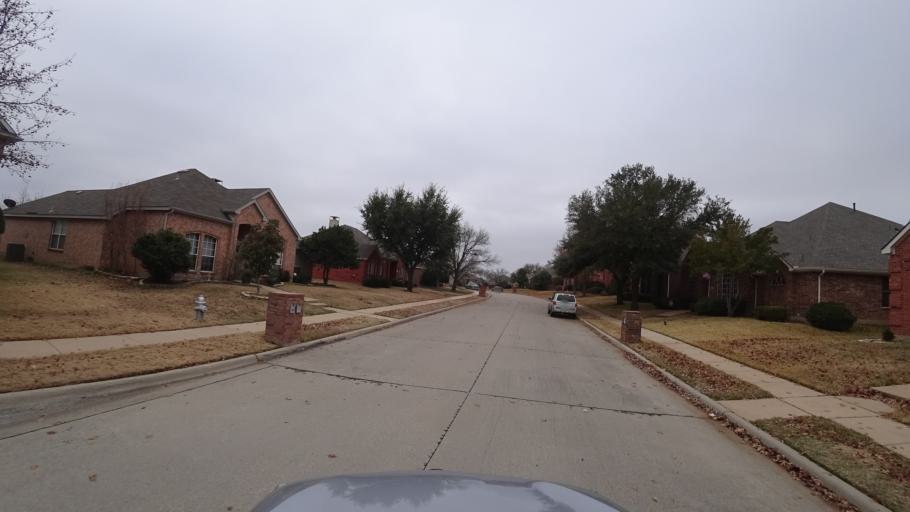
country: US
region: Texas
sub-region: Denton County
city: Highland Village
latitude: 33.0582
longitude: -97.0316
